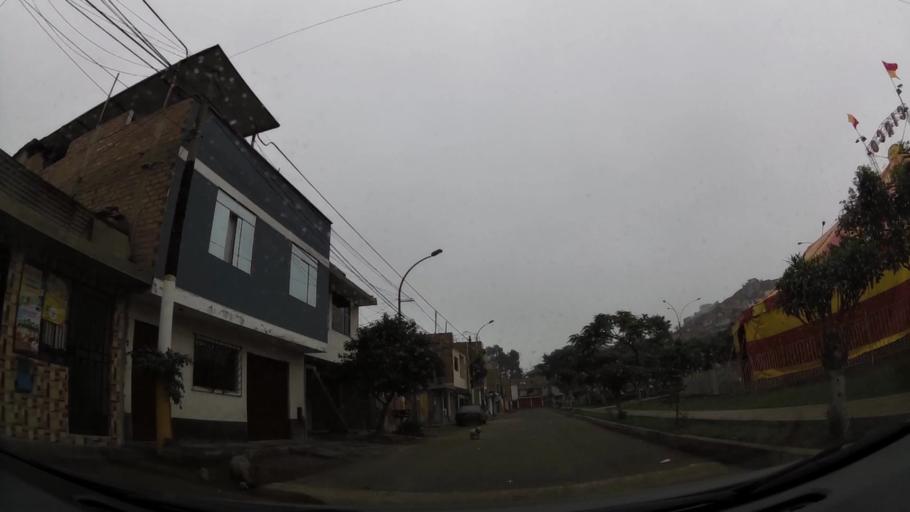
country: PE
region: Lima
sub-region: Lima
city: Carabayllo
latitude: -11.8710
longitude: -77.0748
